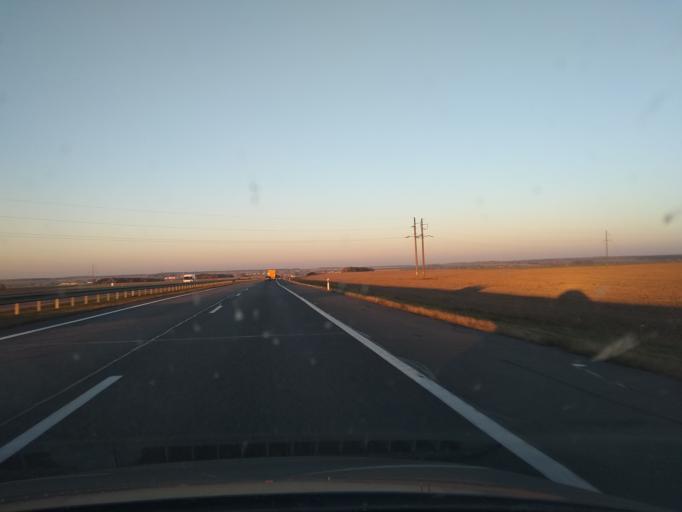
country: BY
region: Minsk
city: Snow
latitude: 53.3238
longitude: 26.4114
